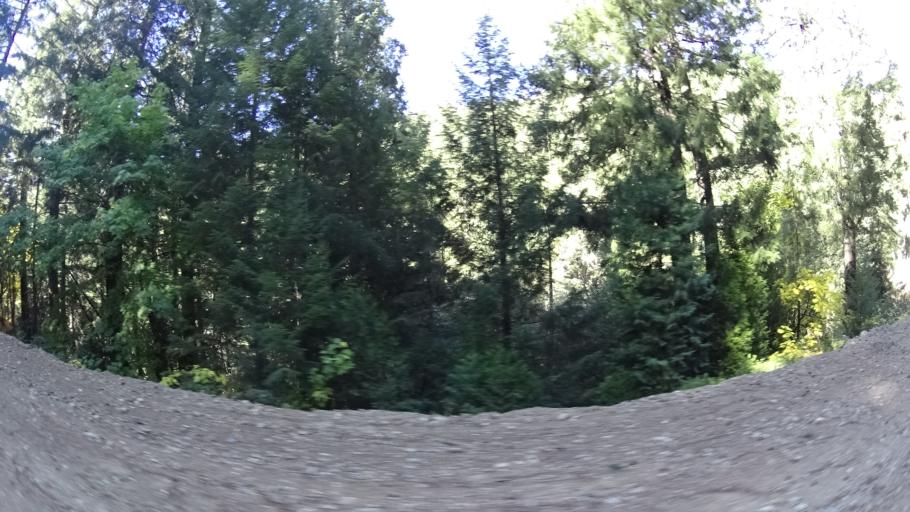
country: US
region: California
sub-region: Trinity County
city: Weaverville
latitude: 41.2271
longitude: -123.0158
